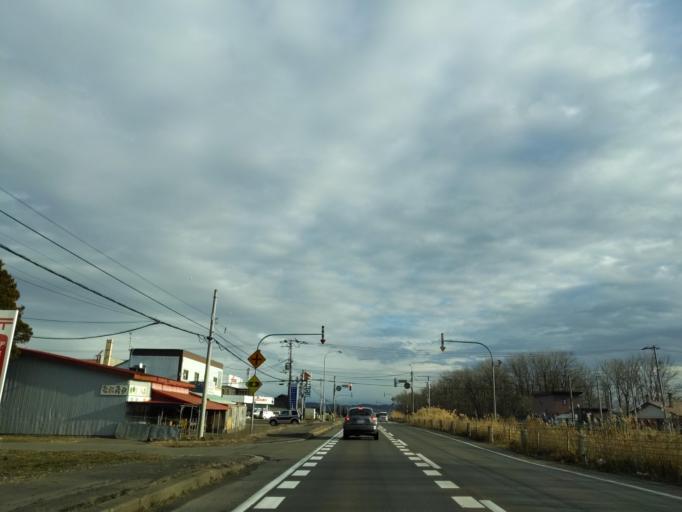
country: JP
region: Hokkaido
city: Kitahiroshima
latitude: 42.9630
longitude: 141.6826
